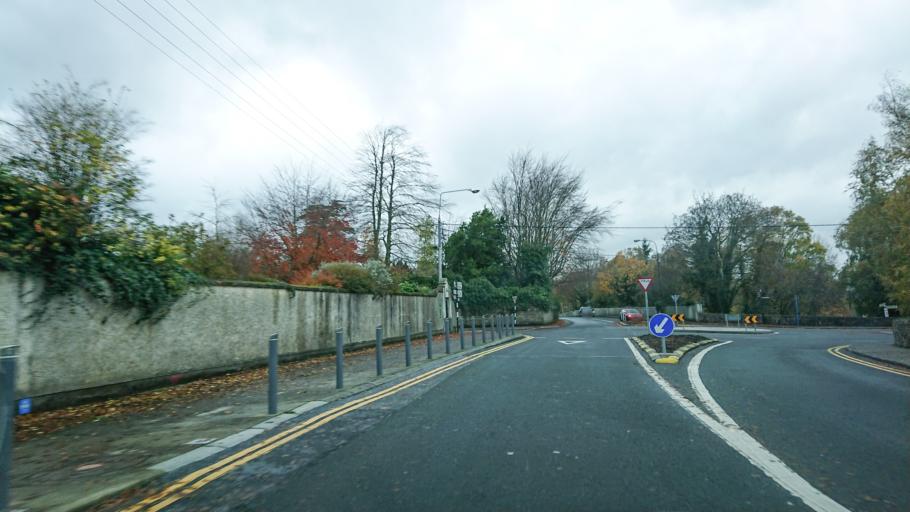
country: IE
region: Munster
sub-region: South Tipperary
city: Cluain Meala
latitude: 52.3512
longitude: -7.6942
